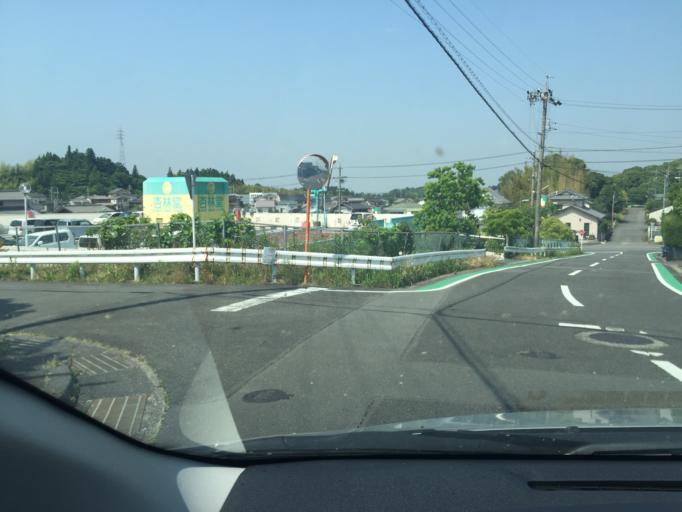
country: JP
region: Shizuoka
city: Kakegawa
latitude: 34.7880
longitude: 138.0287
